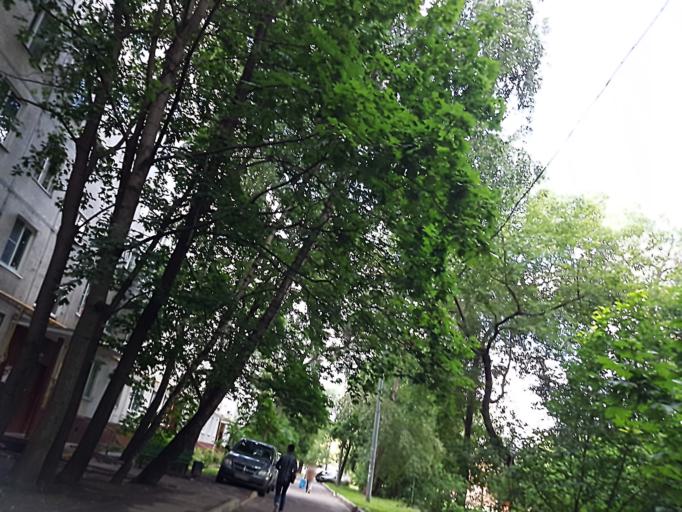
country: RU
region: Moskovskaya
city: Novogireyevo
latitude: 55.7493
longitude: 37.8088
